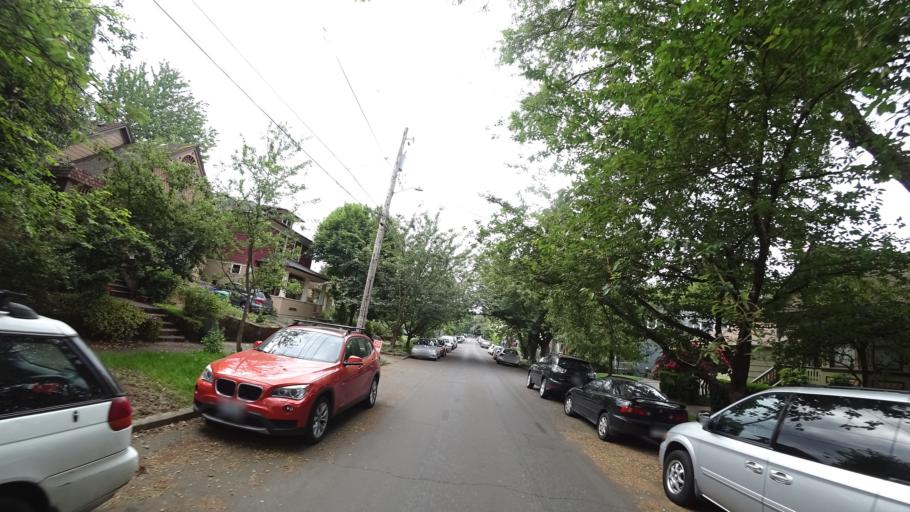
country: US
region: Oregon
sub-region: Multnomah County
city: Portland
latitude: 45.4999
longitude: -122.6407
